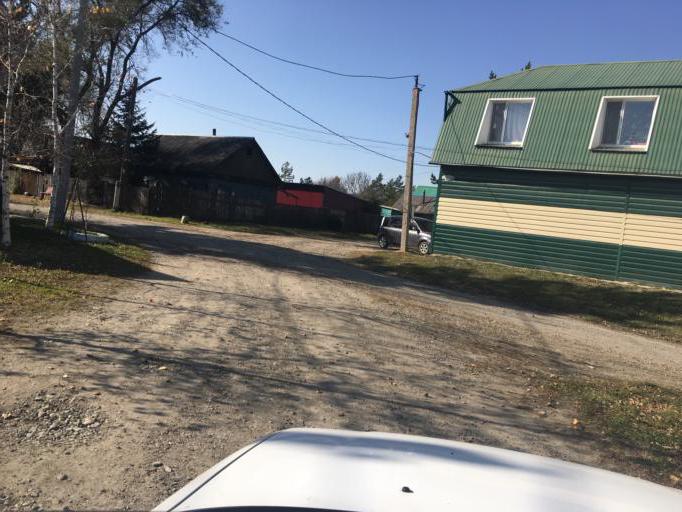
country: RU
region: Primorskiy
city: Dal'nerechensk
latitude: 45.9286
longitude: 133.7515
